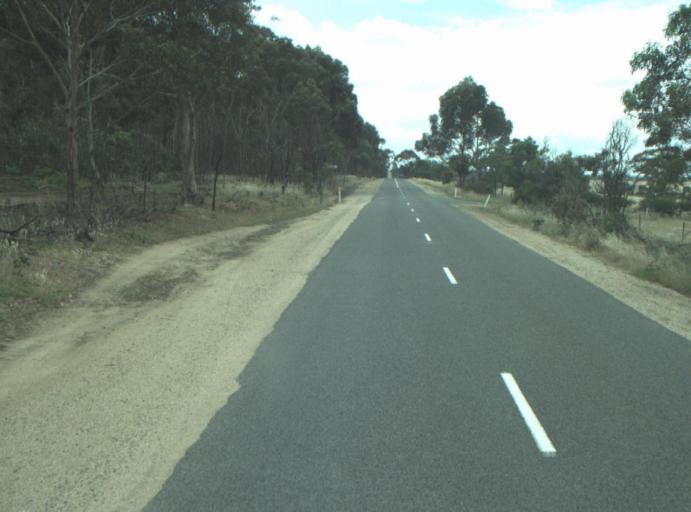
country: AU
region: Victoria
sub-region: Greater Geelong
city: Lara
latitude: -37.9674
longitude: 144.4240
